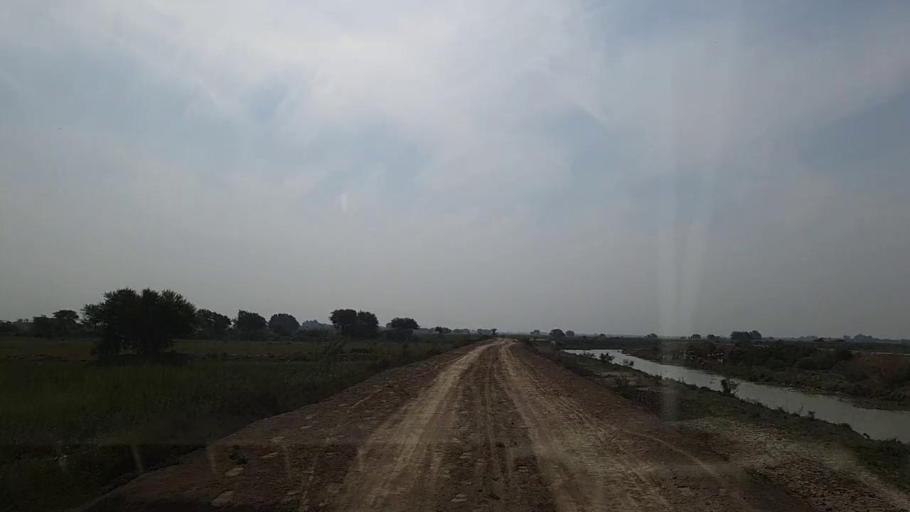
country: PK
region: Sindh
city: Mirpur Batoro
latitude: 24.6634
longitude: 68.2505
